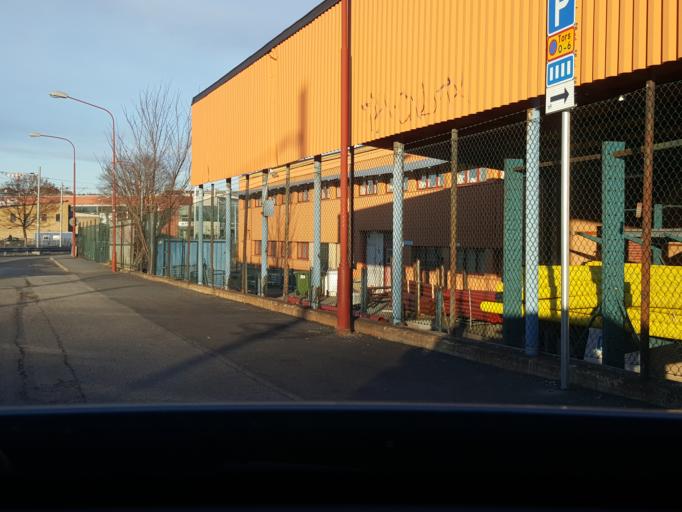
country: SE
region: Stockholm
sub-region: Sundbybergs Kommun
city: Sundbyberg
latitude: 59.3532
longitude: 17.9604
